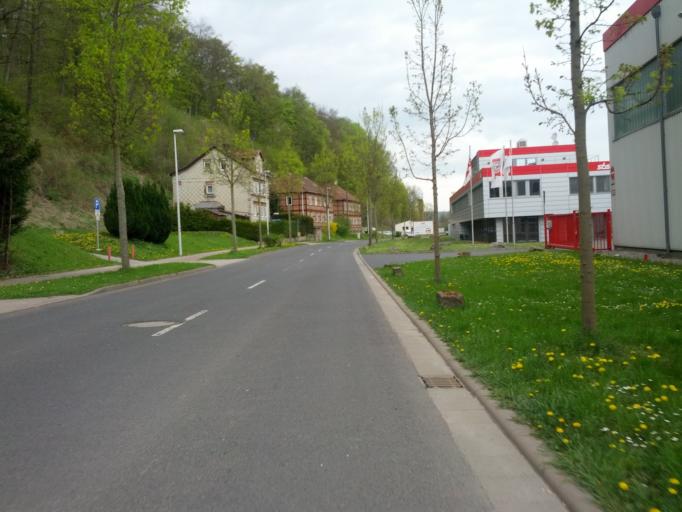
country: DE
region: Thuringia
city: Eisenach
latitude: 50.9685
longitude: 10.3448
